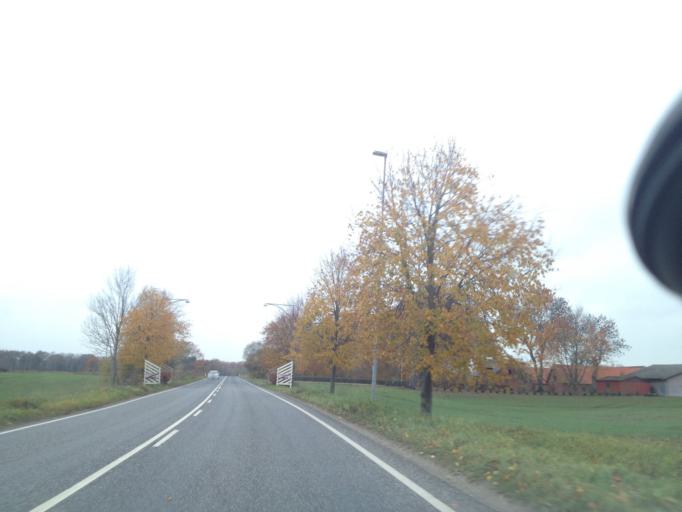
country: DK
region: South Denmark
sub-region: Nordfyns Kommune
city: Sonderso
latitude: 55.4284
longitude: 10.2526
